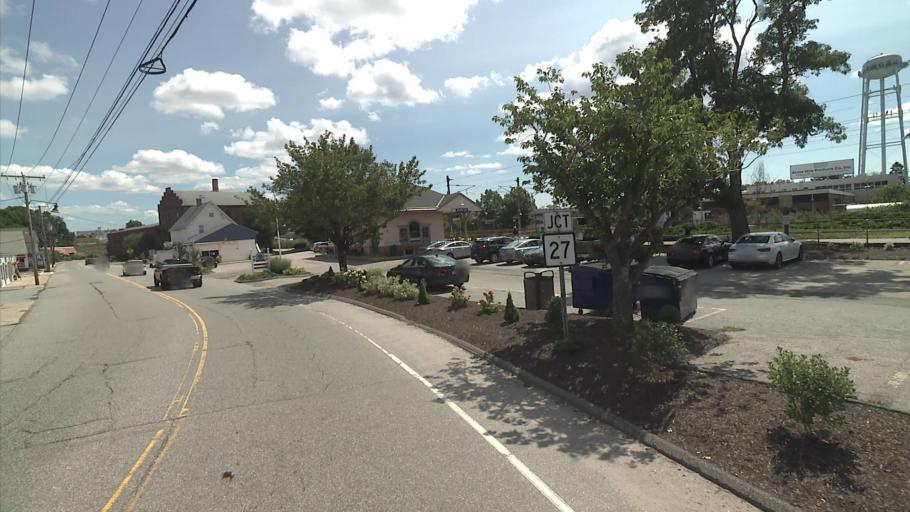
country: US
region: Connecticut
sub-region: New London County
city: Mystic
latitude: 41.3512
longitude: -71.9637
